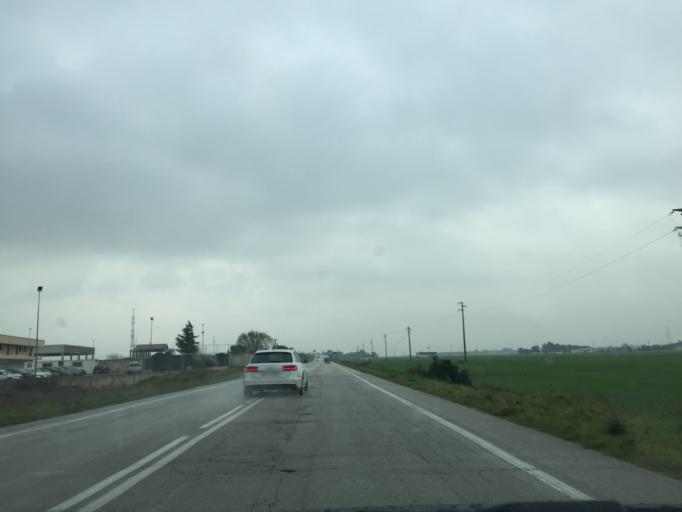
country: IT
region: Apulia
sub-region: Provincia di Foggia
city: Foggia
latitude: 41.4803
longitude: 15.5152
